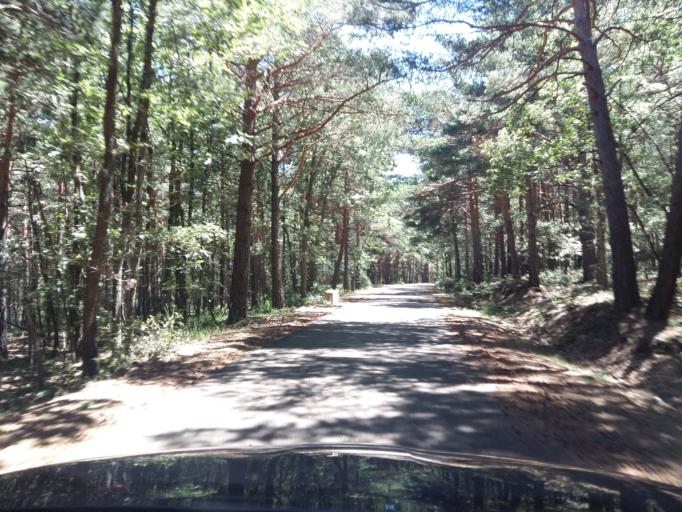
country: ES
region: Castille and Leon
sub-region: Provincia de Soria
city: Vozmediano
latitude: 41.8174
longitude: -1.8262
